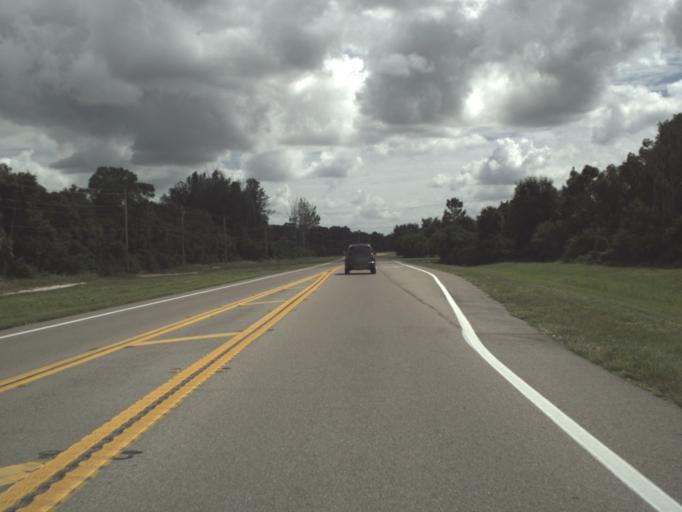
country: US
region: Florida
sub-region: Lee County
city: Lehigh Acres
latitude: 26.5545
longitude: -81.6511
